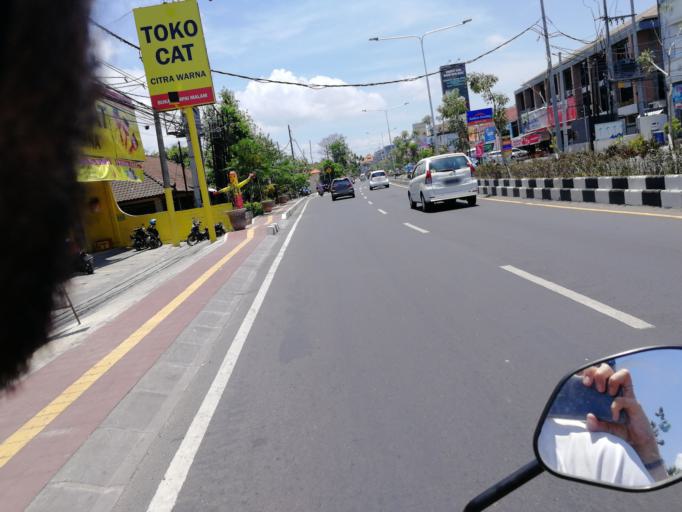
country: ID
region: Bali
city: Kuta
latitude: -8.6969
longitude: 115.1860
